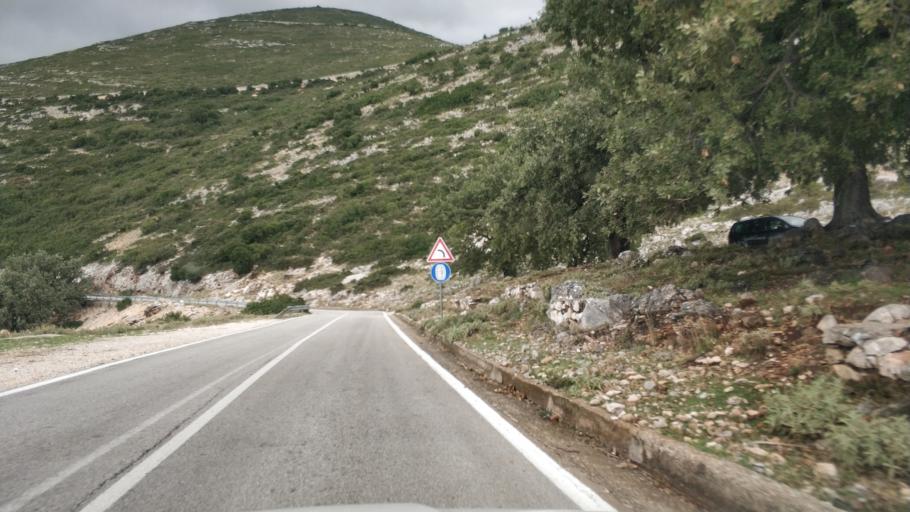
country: AL
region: Vlore
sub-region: Rrethi i Vlores
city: Vranisht
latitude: 40.1763
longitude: 19.6049
